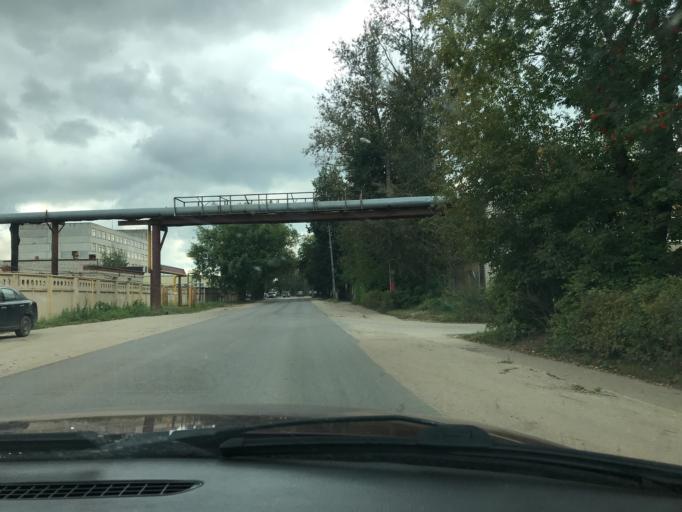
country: RU
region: Kaluga
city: Maloyaroslavets
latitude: 55.0059
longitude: 36.4728
